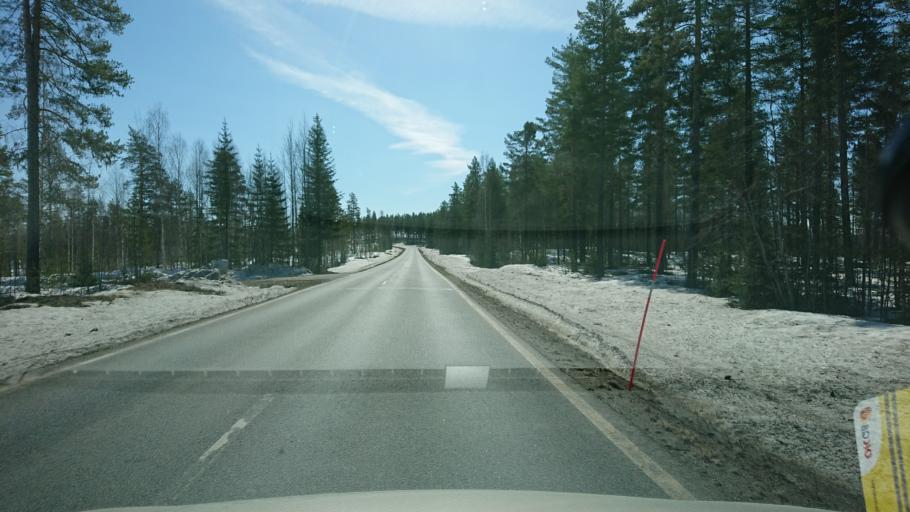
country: SE
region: Vaesterbotten
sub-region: Dorotea Kommun
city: Dorotea
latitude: 64.0287
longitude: 16.2729
